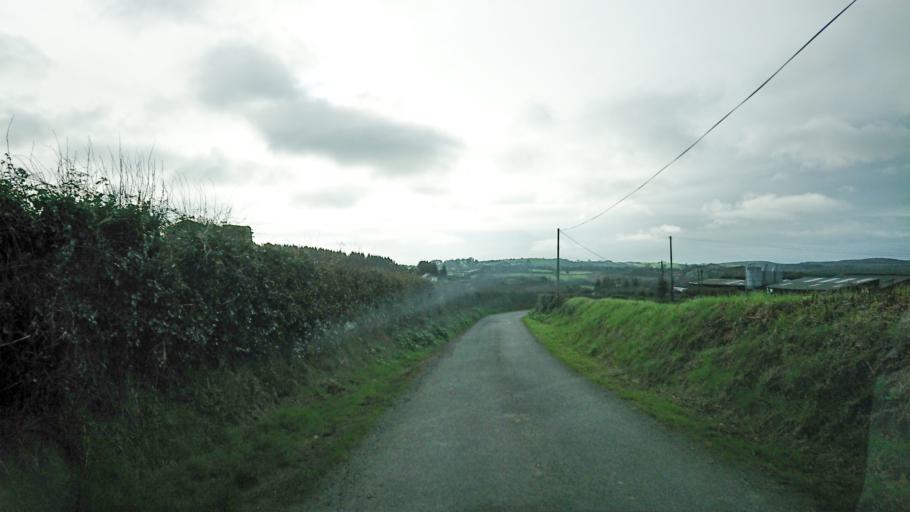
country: IE
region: Munster
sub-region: Waterford
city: Tra Mhor
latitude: 52.1894
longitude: -7.1745
